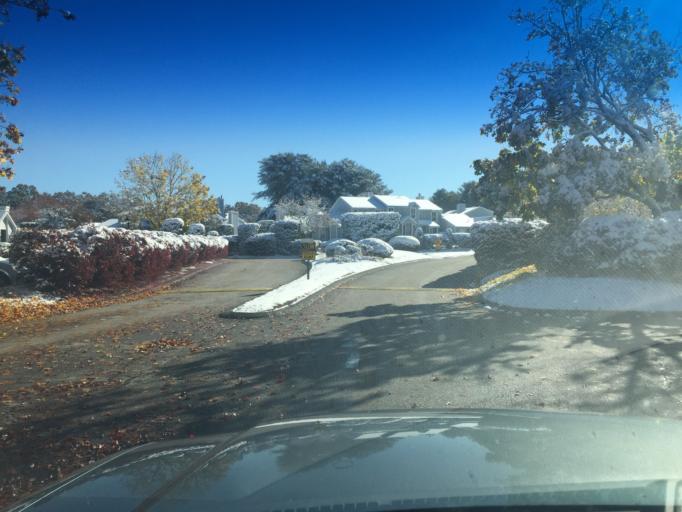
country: US
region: Massachusetts
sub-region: Bristol County
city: Norton
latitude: 41.9440
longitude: -71.1424
